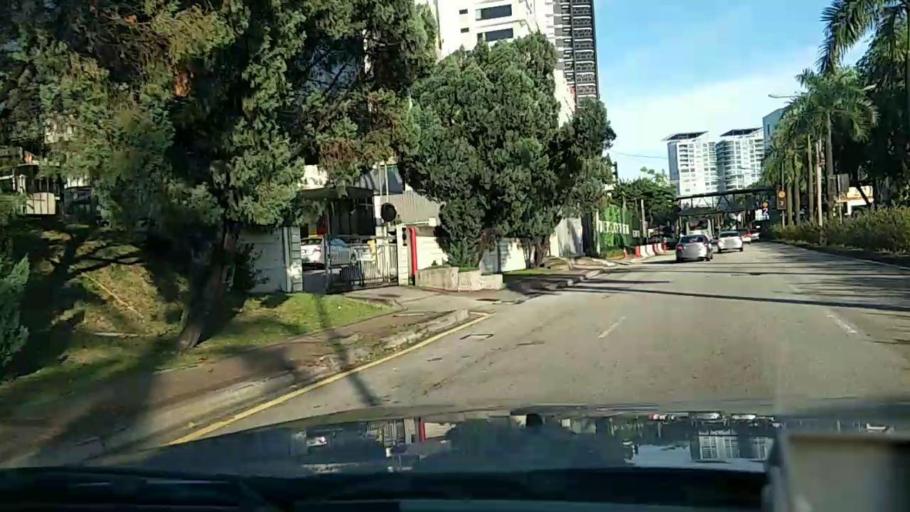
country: MY
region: Selangor
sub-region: Petaling
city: Petaling Jaya
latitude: 3.1115
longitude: 101.6356
